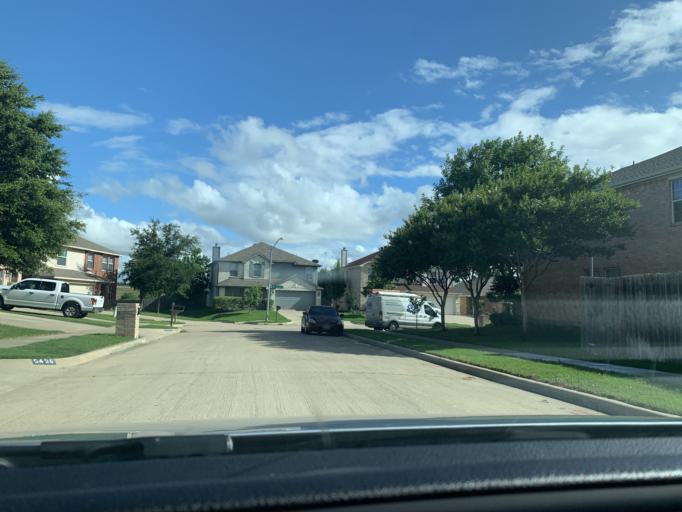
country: US
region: Texas
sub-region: Dallas County
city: Cedar Hill
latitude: 32.6411
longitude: -97.0334
